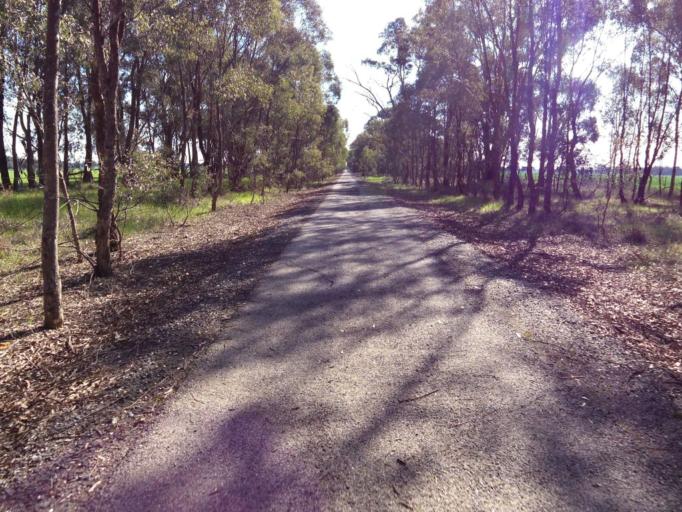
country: AU
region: New South Wales
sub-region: Corowa Shire
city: Corowa
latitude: -36.0251
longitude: 146.4307
